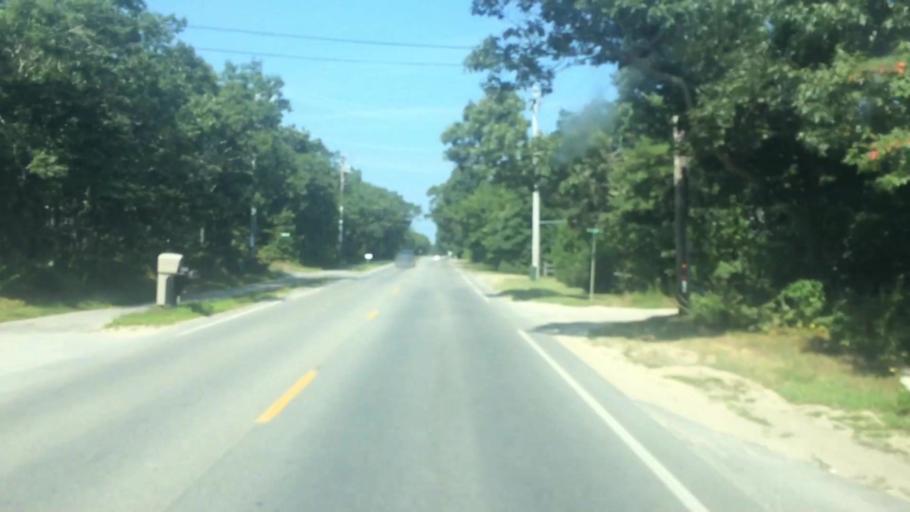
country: US
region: Massachusetts
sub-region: Dukes County
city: Oak Bluffs
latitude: 41.4050
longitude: -70.5601
